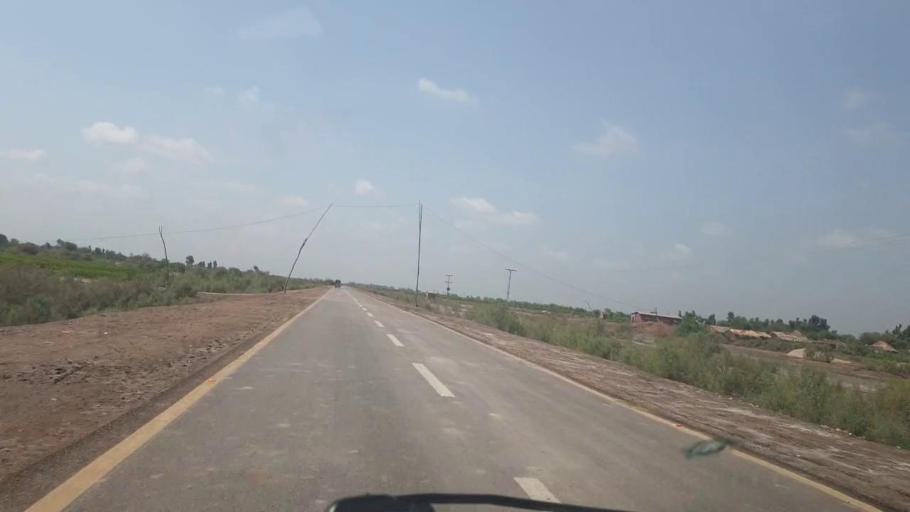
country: PK
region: Sindh
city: Berani
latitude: 25.7246
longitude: 68.9446
